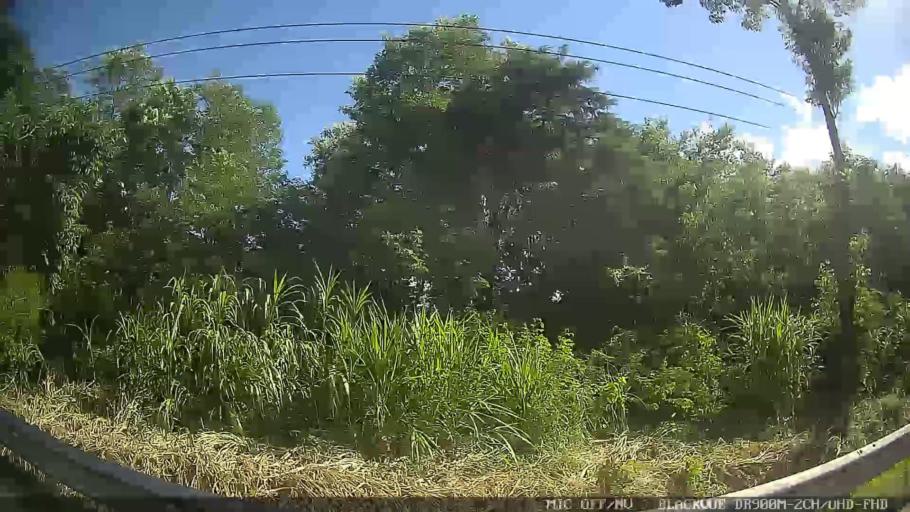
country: BR
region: Sao Paulo
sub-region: Atibaia
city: Atibaia
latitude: -23.1075
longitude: -46.5184
